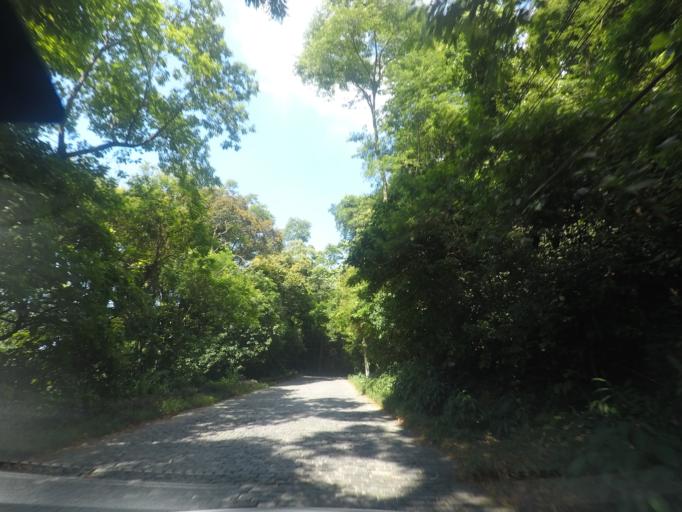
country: BR
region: Rio de Janeiro
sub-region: Petropolis
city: Petropolis
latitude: -22.5501
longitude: -43.1831
